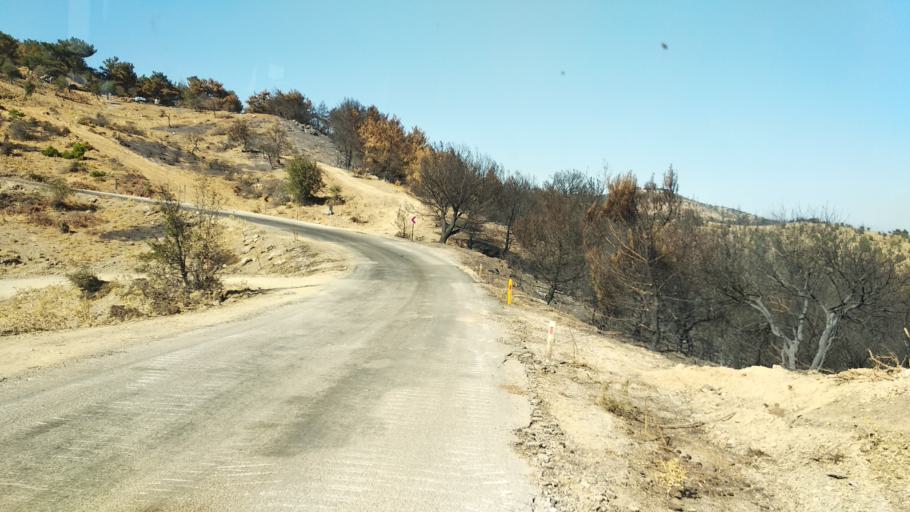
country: TR
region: Izmir
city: Gaziemir
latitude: 38.2942
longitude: 27.0015
